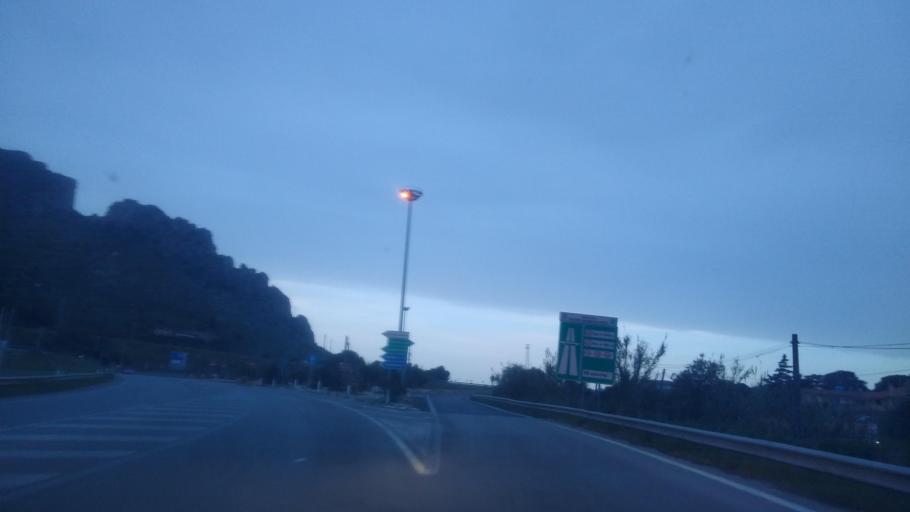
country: IT
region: Sicily
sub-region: Palermo
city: Terrasini
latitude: 38.1388
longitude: 13.0799
